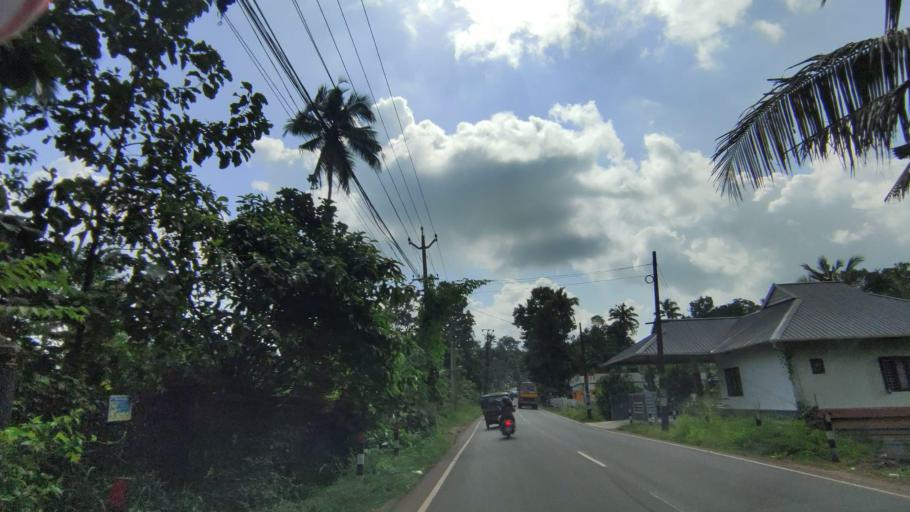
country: IN
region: Kerala
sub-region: Kottayam
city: Kottayam
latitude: 9.6755
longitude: 76.5499
